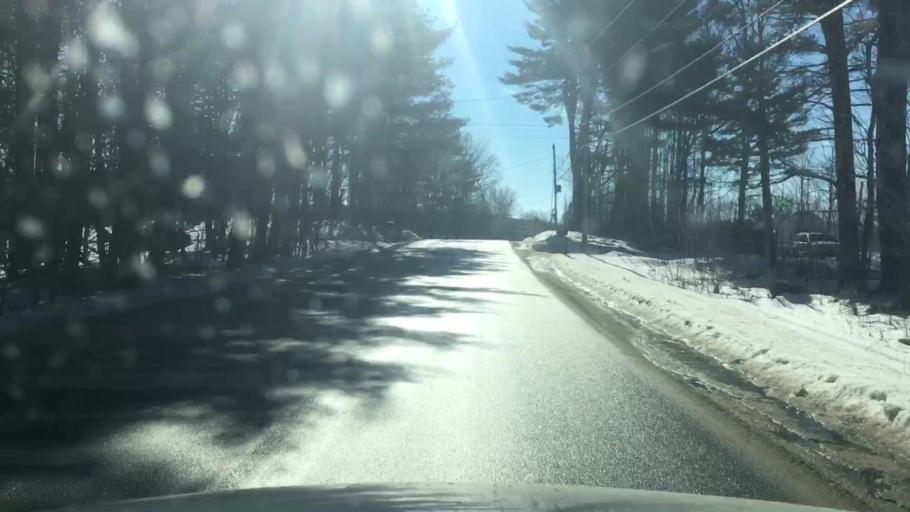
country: US
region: Maine
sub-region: Cumberland County
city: New Gloucester
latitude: 43.8725
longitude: -70.3334
